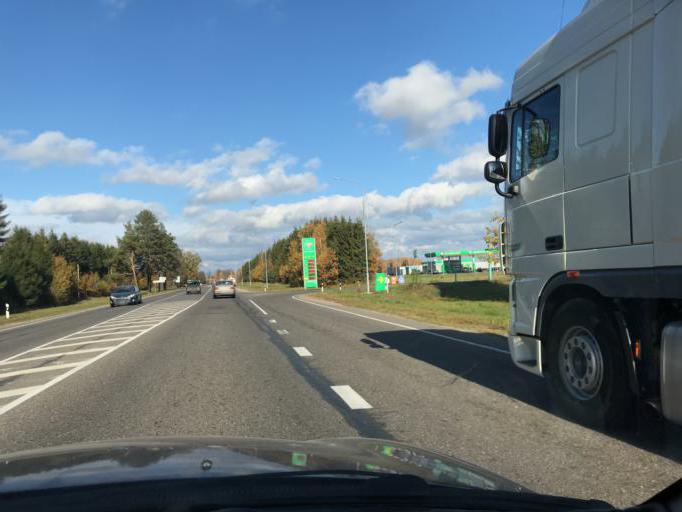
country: LT
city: Salcininkai
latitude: 54.2326
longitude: 25.3576
